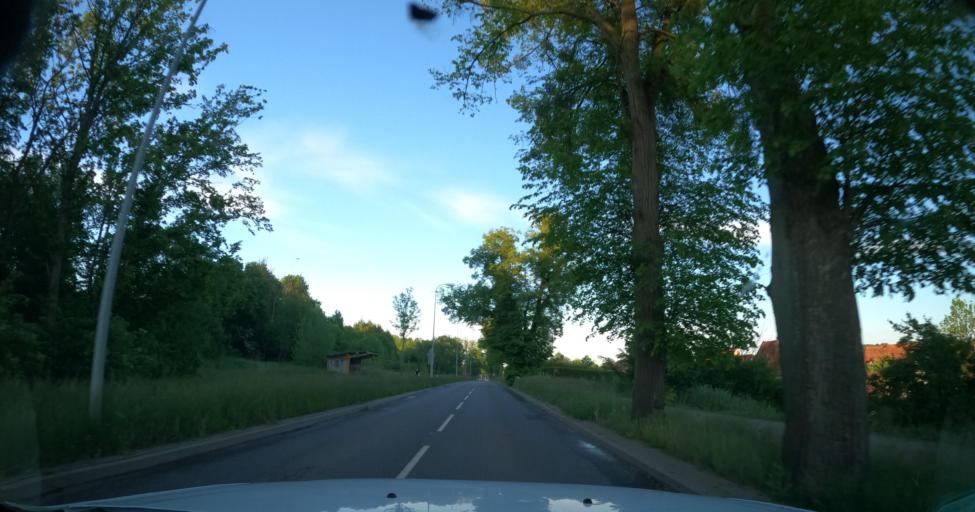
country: PL
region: Warmian-Masurian Voivodeship
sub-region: Powiat lidzbarski
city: Lidzbark Warminski
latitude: 54.1257
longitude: 20.5478
